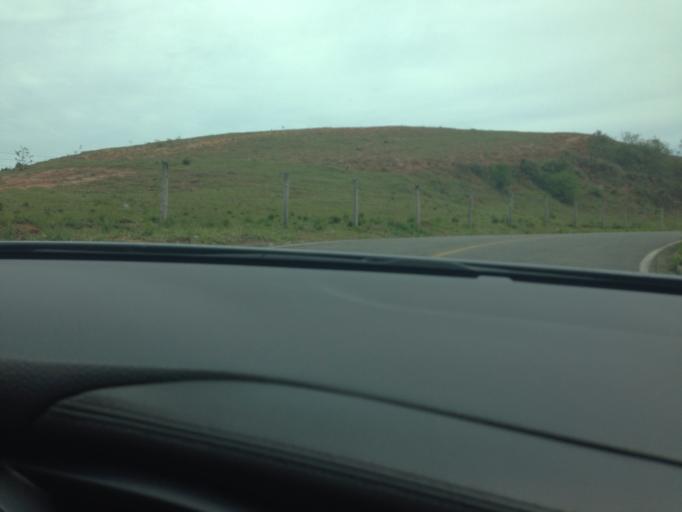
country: BR
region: Espirito Santo
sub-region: Guarapari
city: Guarapari
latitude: -20.6245
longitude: -40.5278
